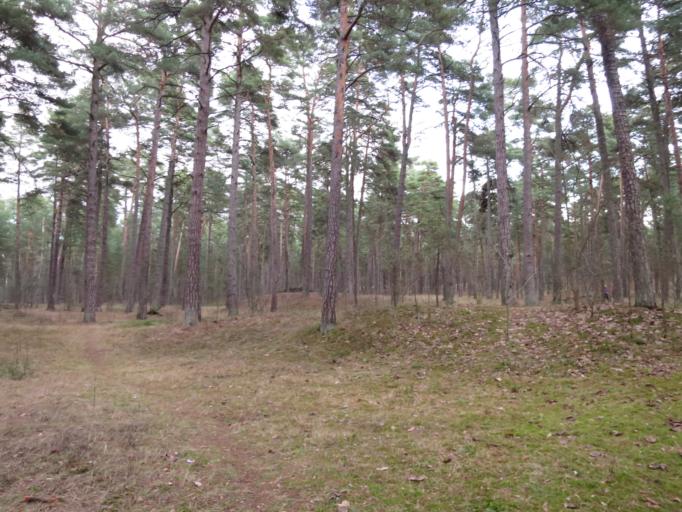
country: LV
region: Riga
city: Bolderaja
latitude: 57.0412
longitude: 24.0946
